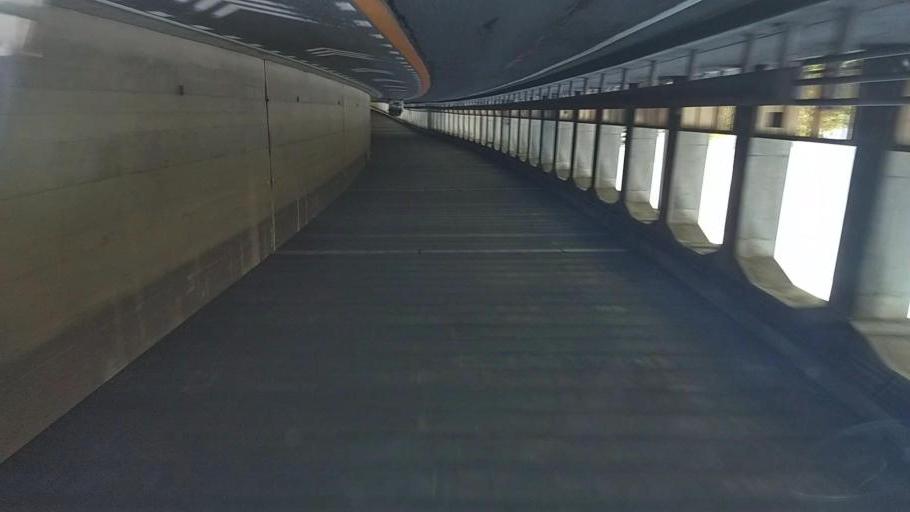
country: JP
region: Yamanashi
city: Ryuo
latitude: 35.5031
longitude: 138.4462
